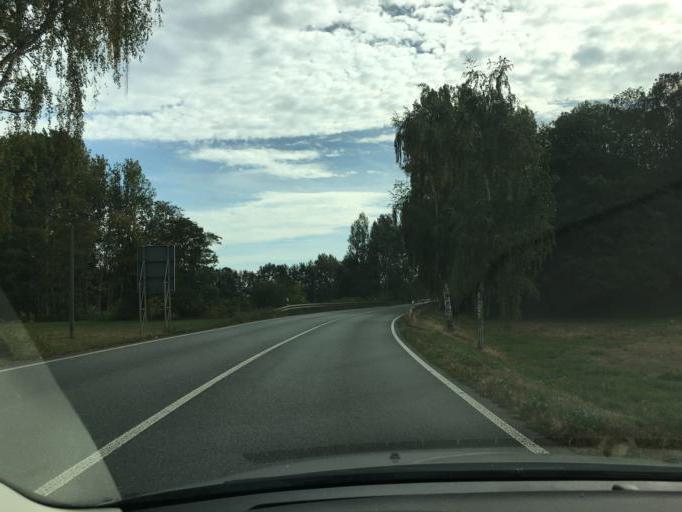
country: DE
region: Saxony
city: Stauchitz
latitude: 51.2678
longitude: 13.2577
